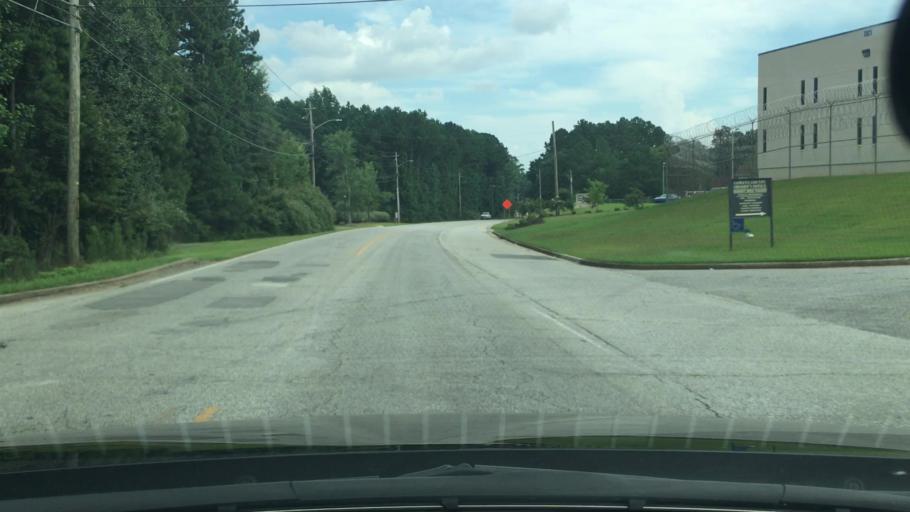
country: US
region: Georgia
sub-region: Coweta County
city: Newnan
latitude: 33.3828
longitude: -84.7828
